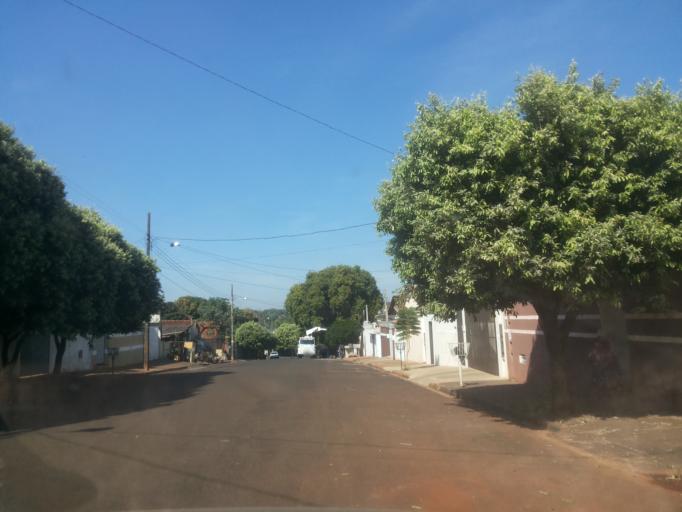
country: BR
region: Minas Gerais
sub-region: Ituiutaba
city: Ituiutaba
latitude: -18.9698
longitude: -49.4527
